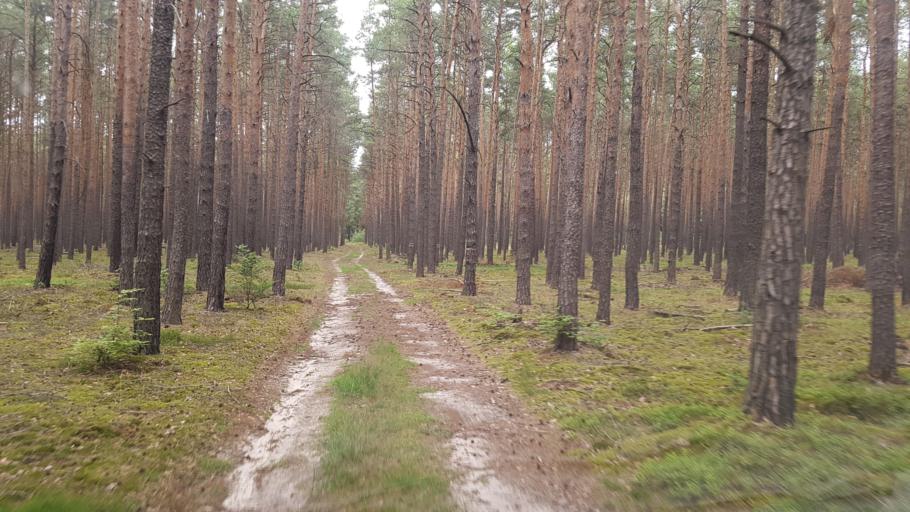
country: DE
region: Brandenburg
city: Crinitz
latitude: 51.7284
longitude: 13.7410
